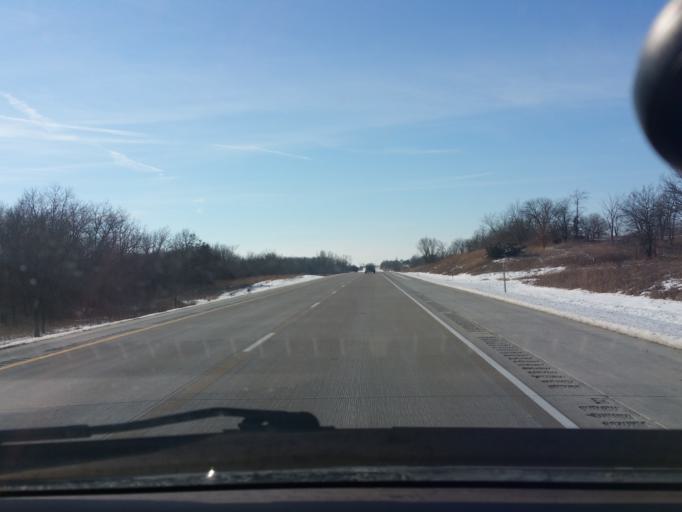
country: US
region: Iowa
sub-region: Decatur County
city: Lamoni
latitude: 40.6034
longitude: -93.9101
